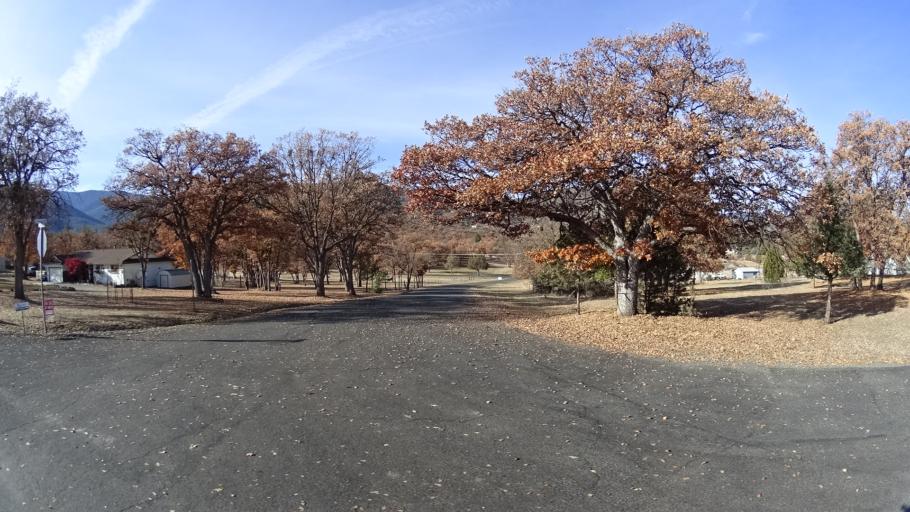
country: US
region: California
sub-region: Siskiyou County
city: Yreka
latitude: 41.6673
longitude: -122.6216
